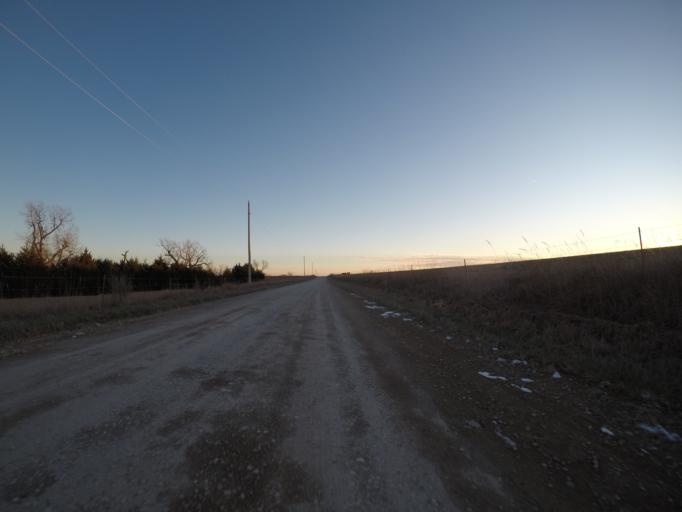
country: US
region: Kansas
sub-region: Riley County
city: Manhattan
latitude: 39.2717
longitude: -96.4823
